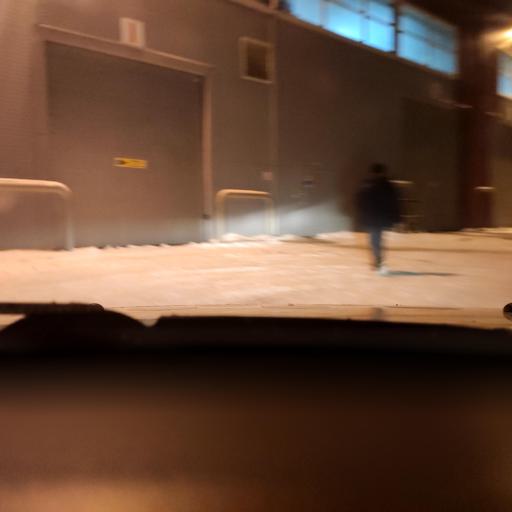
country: RU
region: Perm
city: Froly
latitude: 57.9595
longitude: 56.2699
